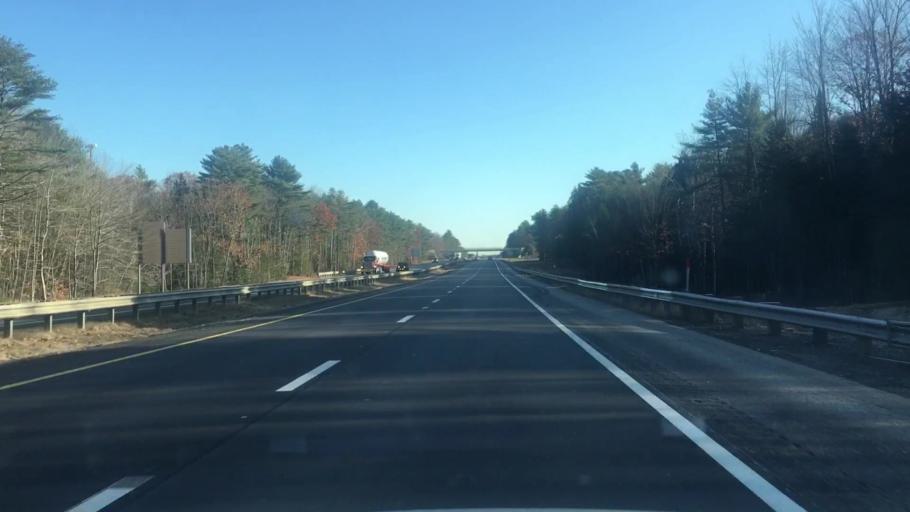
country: US
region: Maine
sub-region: Androscoggin County
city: Auburn
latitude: 44.0452
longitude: -70.2460
